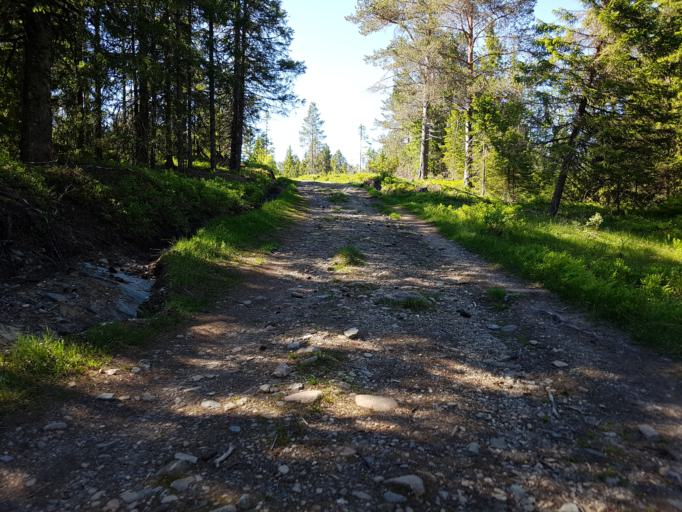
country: NO
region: Sor-Trondelag
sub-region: Trondheim
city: Trondheim
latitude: 63.4266
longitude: 10.2987
